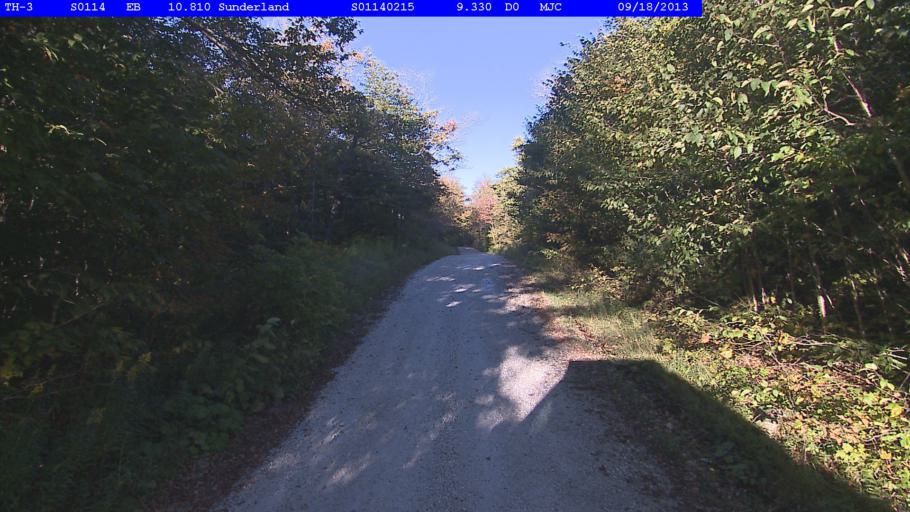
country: US
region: Vermont
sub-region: Bennington County
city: Manchester Center
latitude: 43.0580
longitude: -73.0086
